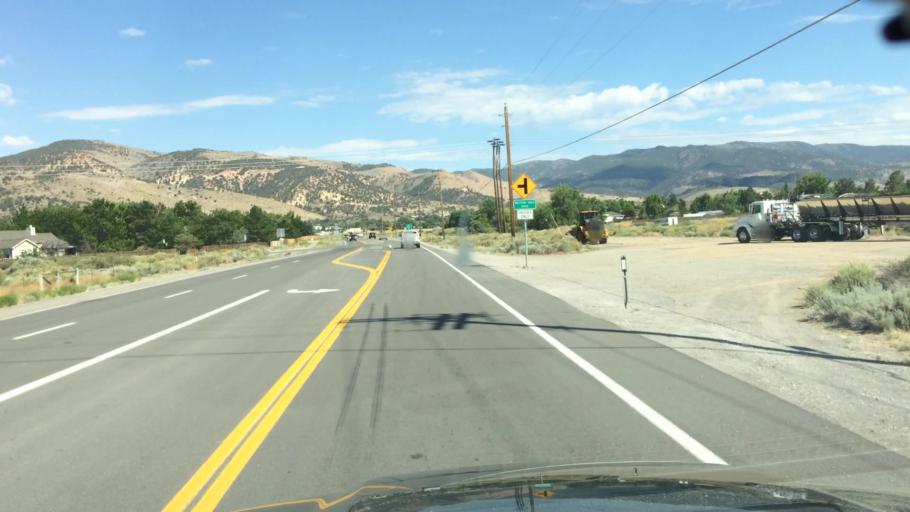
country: US
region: Nevada
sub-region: Storey County
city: Virginia City
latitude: 39.3976
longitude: -119.7354
